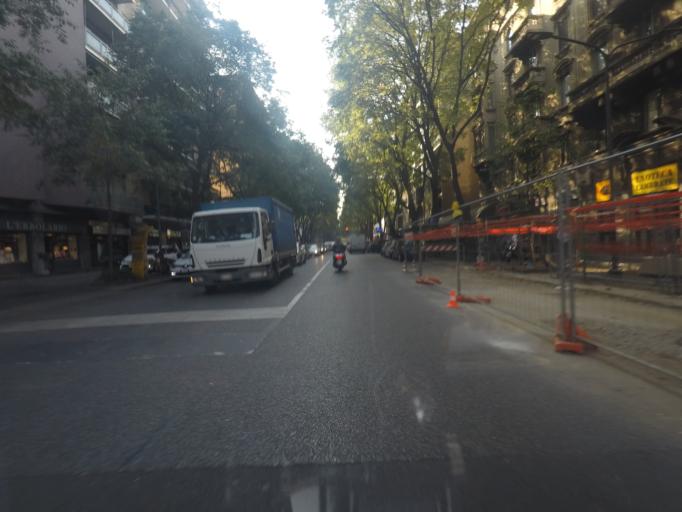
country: IT
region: Lombardy
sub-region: Citta metropolitana di Milano
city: Milano
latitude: 45.4860
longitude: 9.2299
